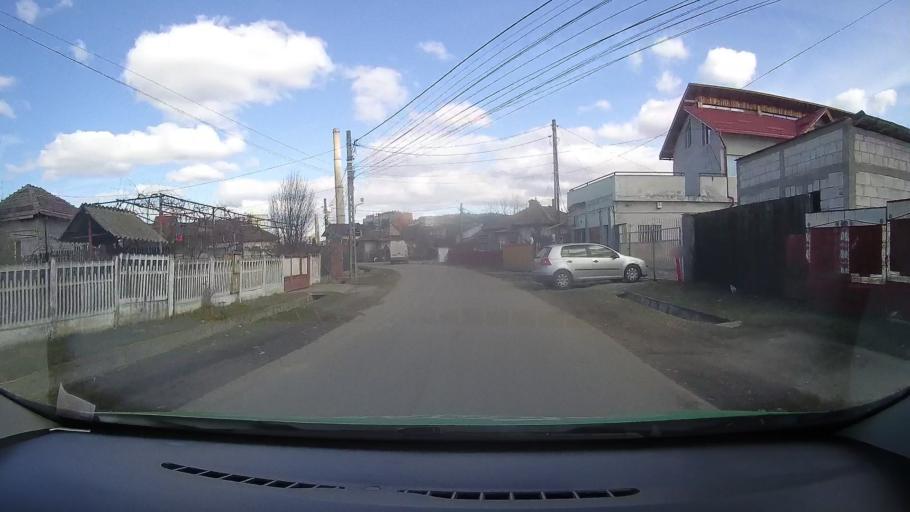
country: RO
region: Dambovita
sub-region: Comuna Doicesti
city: Doicesti
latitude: 44.9948
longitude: 25.3922
